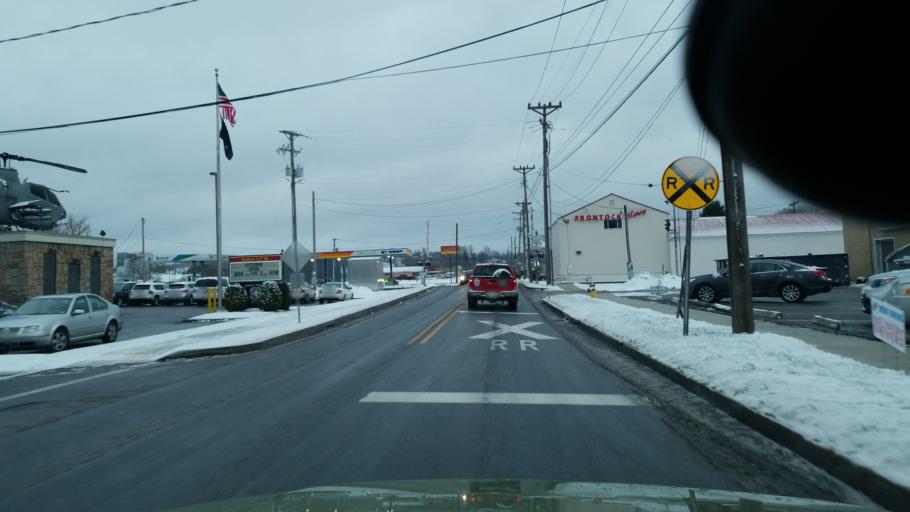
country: US
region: Pennsylvania
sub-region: Clearfield County
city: DuBois
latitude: 41.1245
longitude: -78.7671
